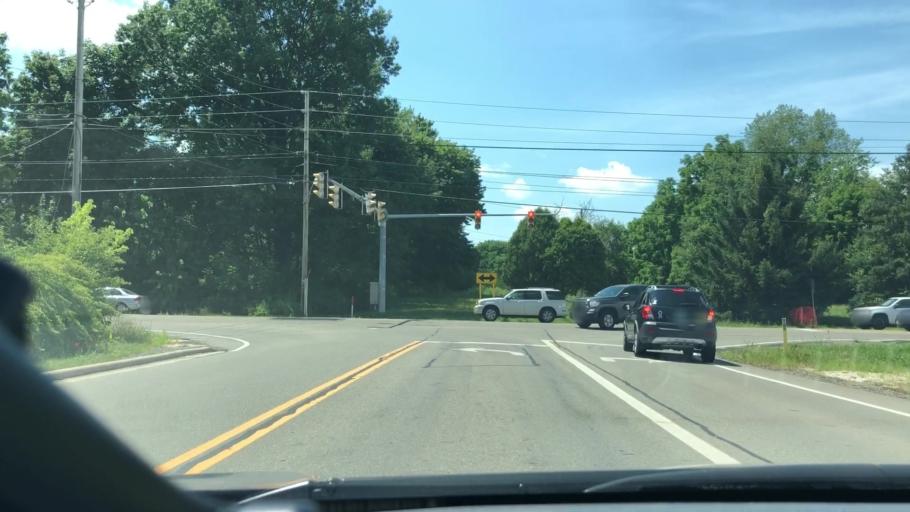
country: US
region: Ohio
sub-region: Summit County
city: Green
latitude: 40.9601
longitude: -81.4936
